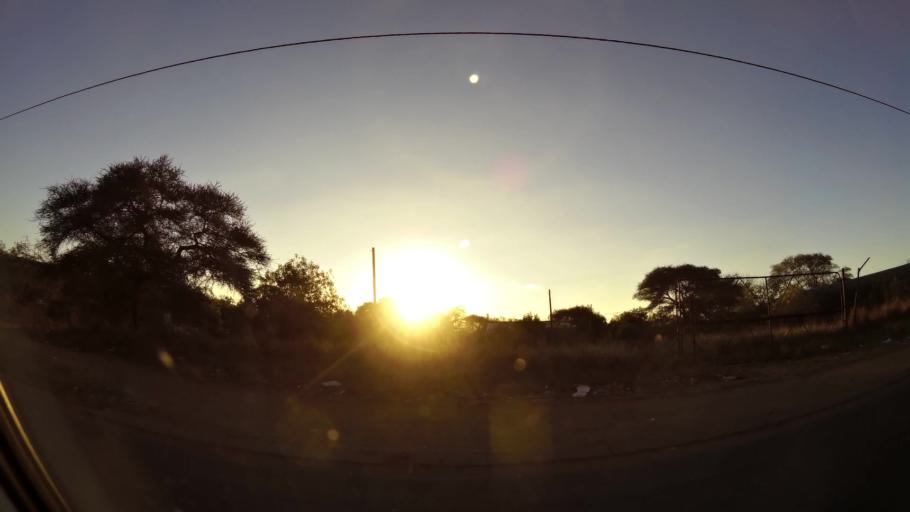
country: ZA
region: Limpopo
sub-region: Waterberg District Municipality
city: Mokopane
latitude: -24.1424
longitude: 28.9751
